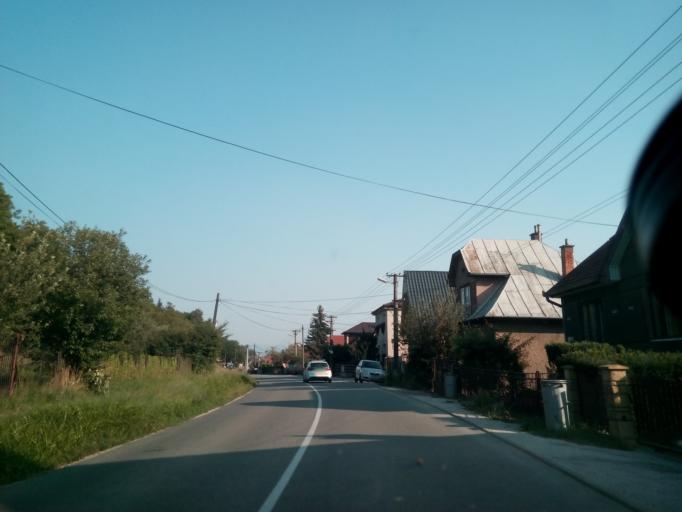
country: SK
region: Kosicky
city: Kosice
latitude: 48.7132
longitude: 21.1985
